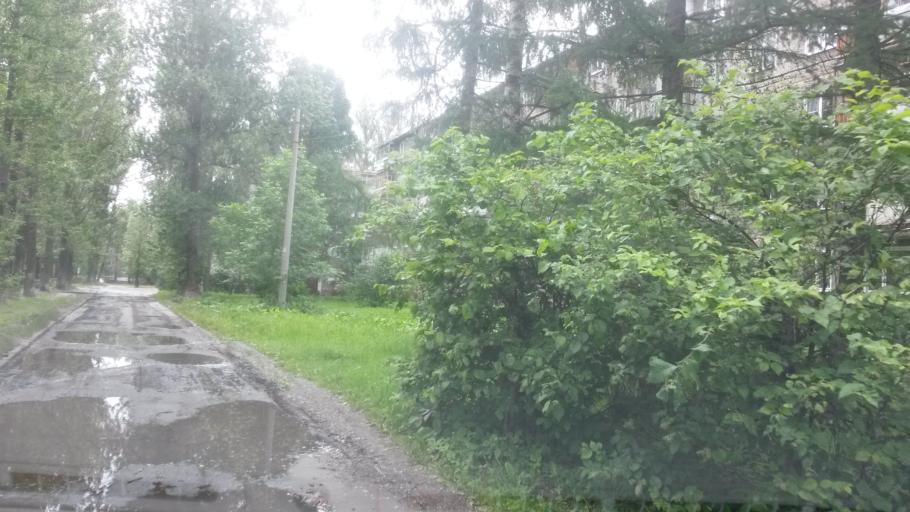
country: RU
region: Jaroslavl
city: Yaroslavl
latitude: 57.6839
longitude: 39.7745
